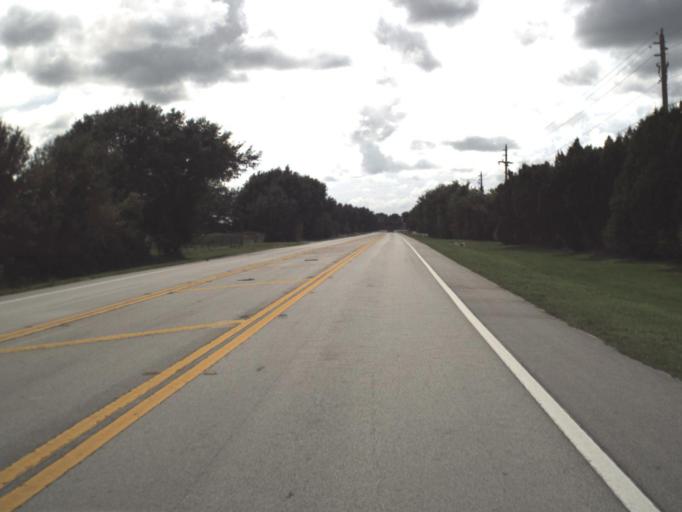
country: US
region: Florida
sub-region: DeSoto County
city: Nocatee
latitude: 27.2055
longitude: -81.9235
